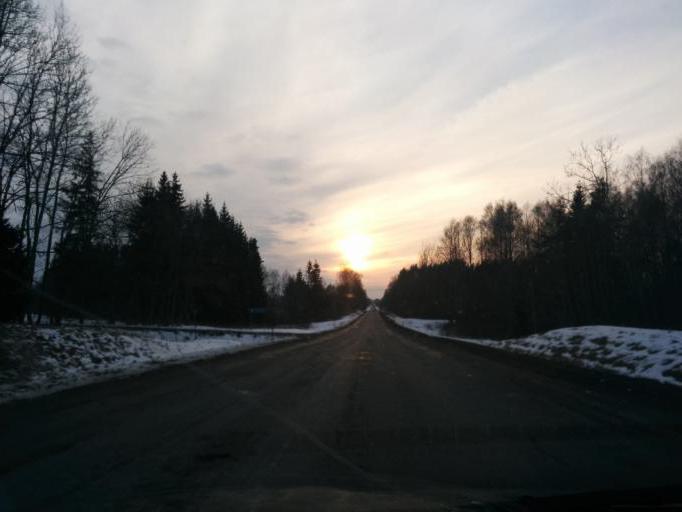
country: LV
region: Priekuli
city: Priekuli
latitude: 57.2652
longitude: 25.4243
